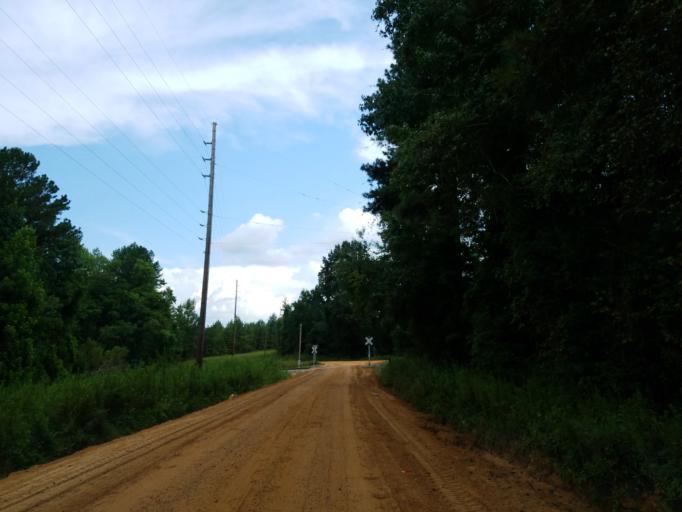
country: US
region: Georgia
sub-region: Dooly County
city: Unadilla
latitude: 32.2885
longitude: -83.7180
